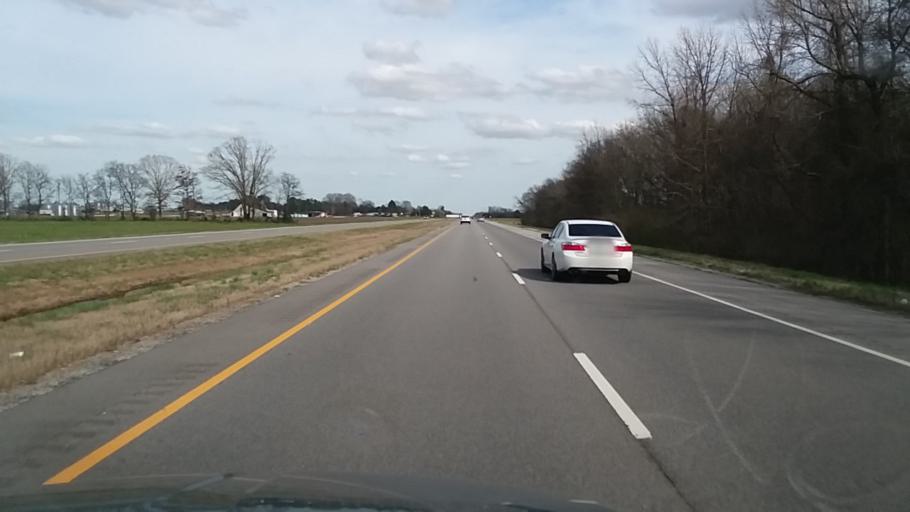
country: US
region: Alabama
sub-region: Colbert County
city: Muscle Shoals
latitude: 34.6848
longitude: -87.5749
